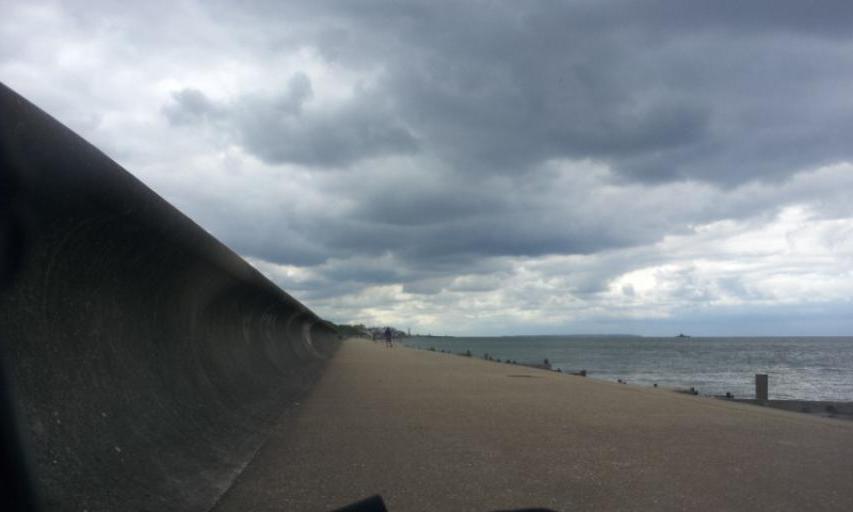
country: GB
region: England
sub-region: Kent
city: Herne Bay
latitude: 51.3735
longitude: 1.1553
